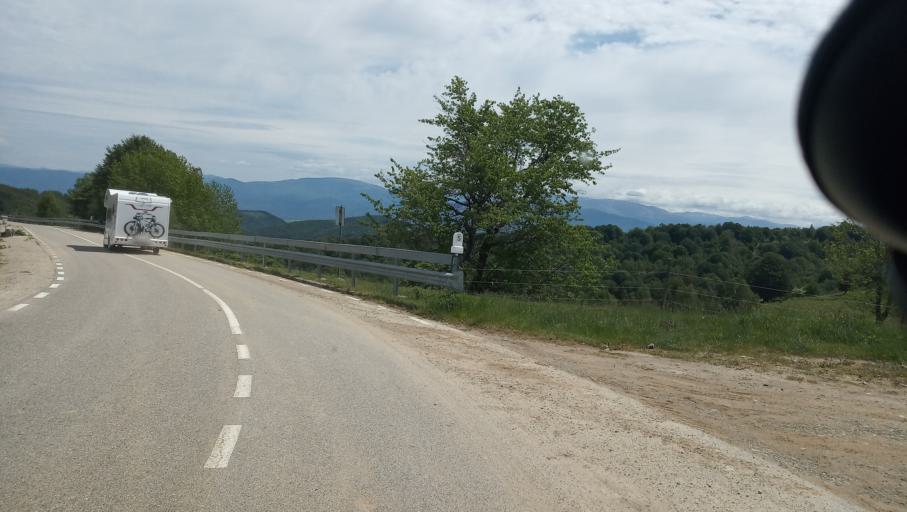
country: RO
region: Caras-Severin
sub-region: Comuna Brebu Nou
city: Brebu Nou
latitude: 45.2404
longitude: 22.1581
